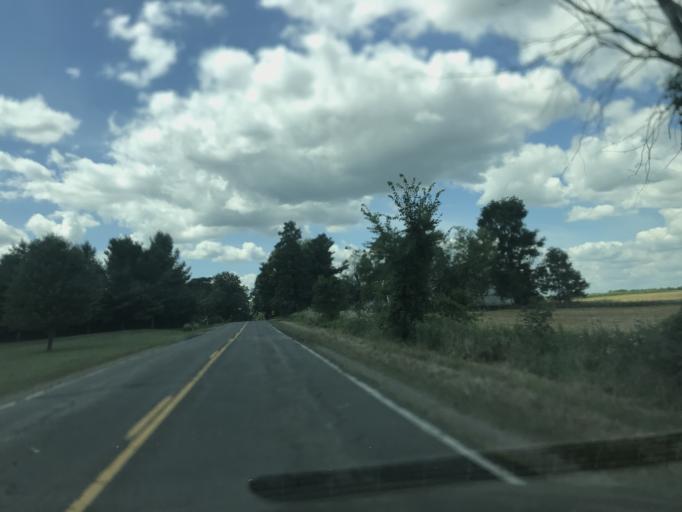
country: US
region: Michigan
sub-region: Ingham County
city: Leslie
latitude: 42.4510
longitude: -84.5224
